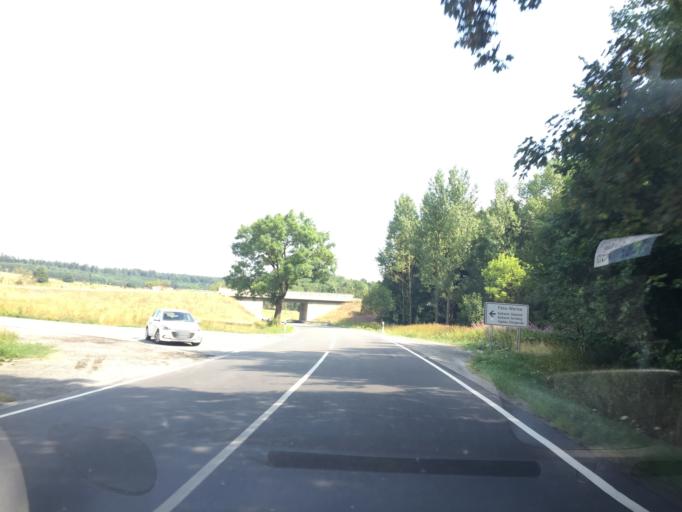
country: DE
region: Saxony-Anhalt
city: Elbingerode
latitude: 51.7592
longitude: 10.7835
